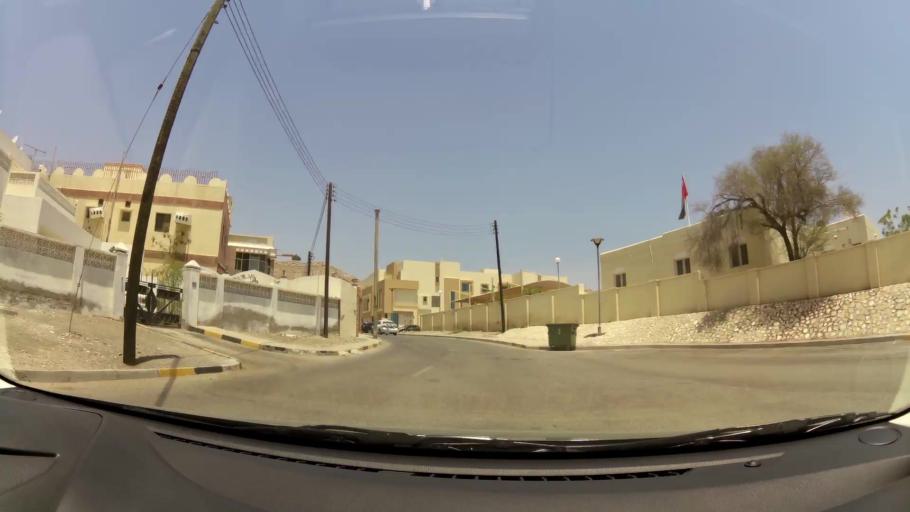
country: OM
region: Muhafazat Masqat
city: Muscat
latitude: 23.6040
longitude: 58.5401
